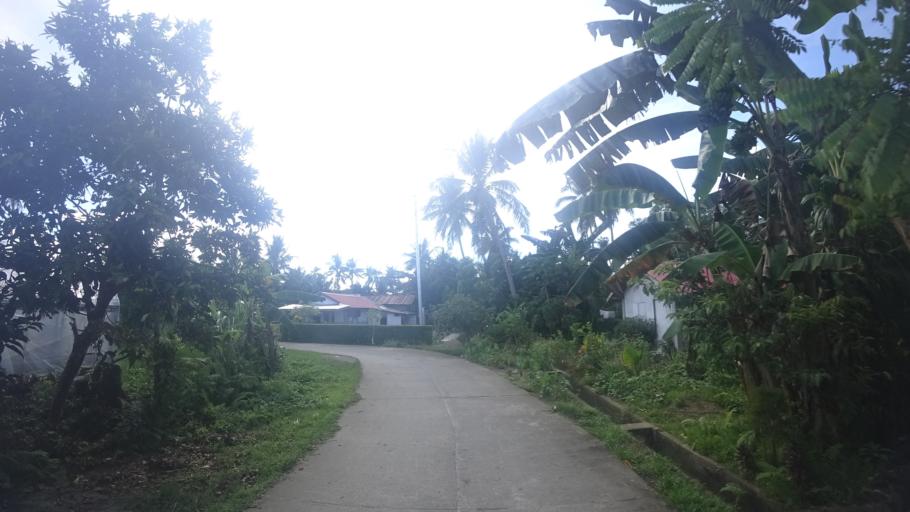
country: PH
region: Eastern Visayas
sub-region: Province of Leyte
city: Pastrana
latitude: 11.1548
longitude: 124.8597
